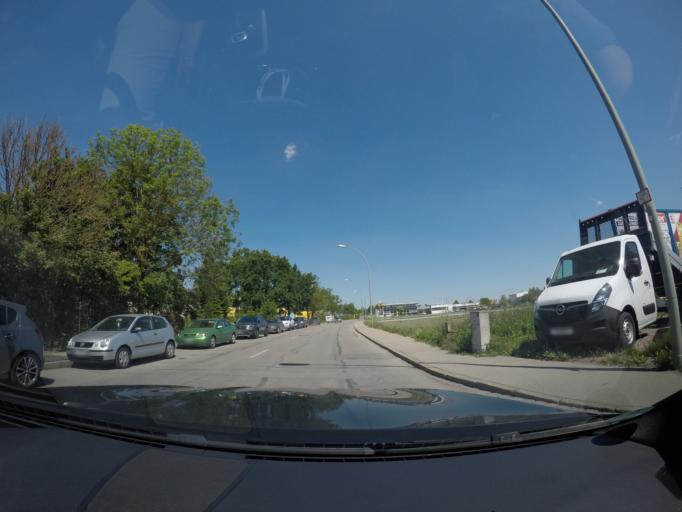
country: DE
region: Bavaria
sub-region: Lower Bavaria
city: Tiefenbach
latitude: 48.5361
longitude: 12.1202
